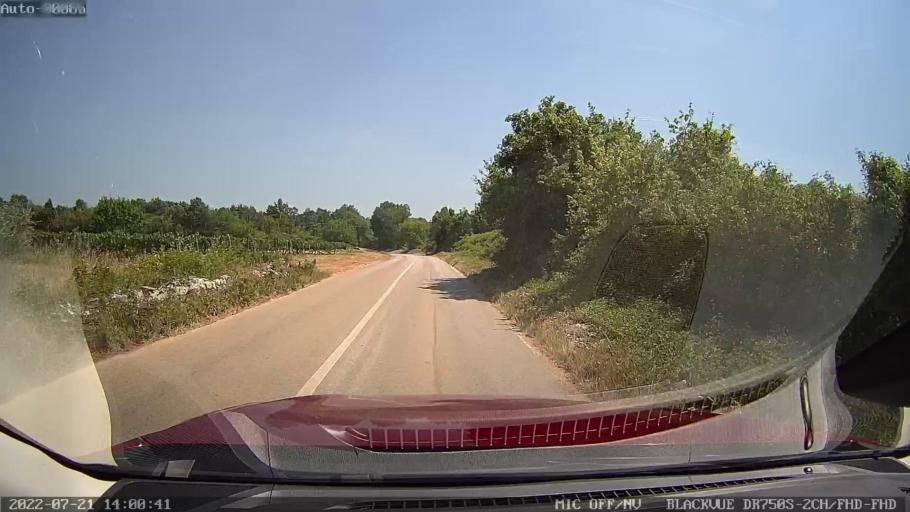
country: HR
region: Istarska
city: Vodnjan
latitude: 45.0969
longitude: 13.8718
